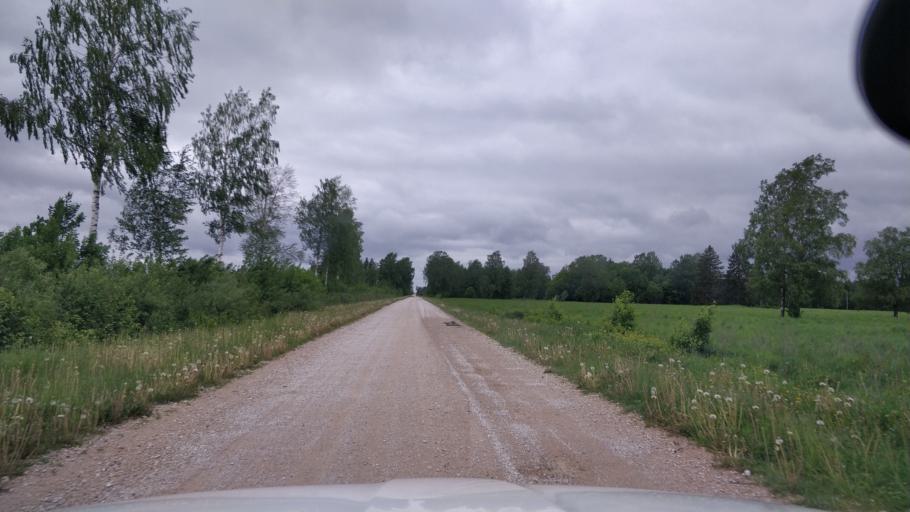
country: EE
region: Raplamaa
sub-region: Maerjamaa vald
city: Marjamaa
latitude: 58.7165
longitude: 24.2768
